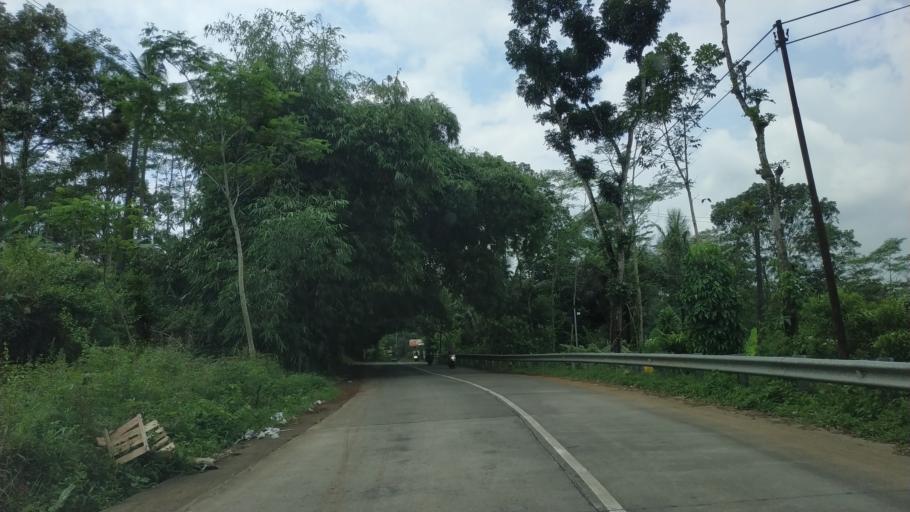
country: ID
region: Central Java
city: Weleri
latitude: -7.1049
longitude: 110.0741
